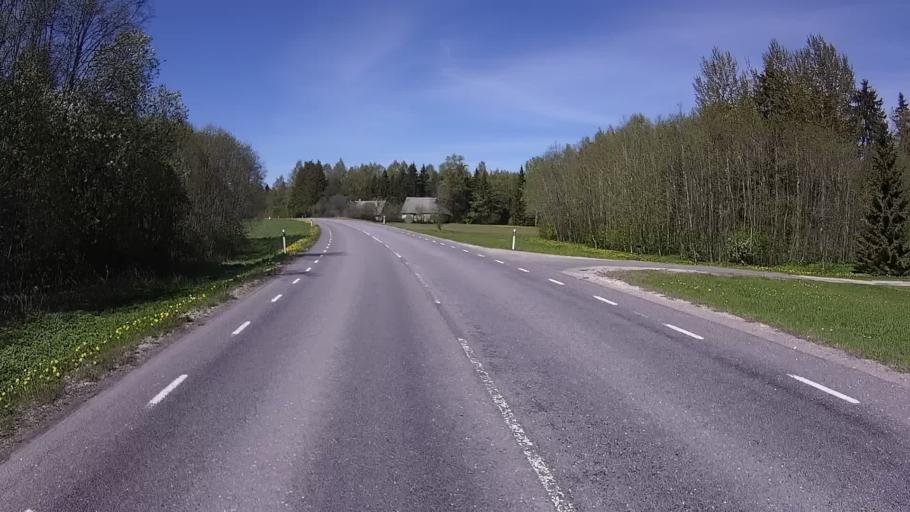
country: EE
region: Raplamaa
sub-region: Kehtna vald
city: Kehtna
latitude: 59.0522
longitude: 25.0204
